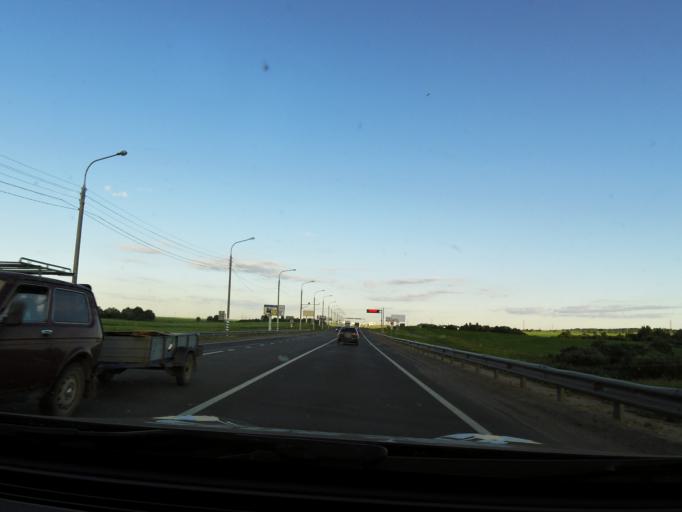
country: RU
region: Vologda
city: Vologda
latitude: 59.1705
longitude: 39.9096
